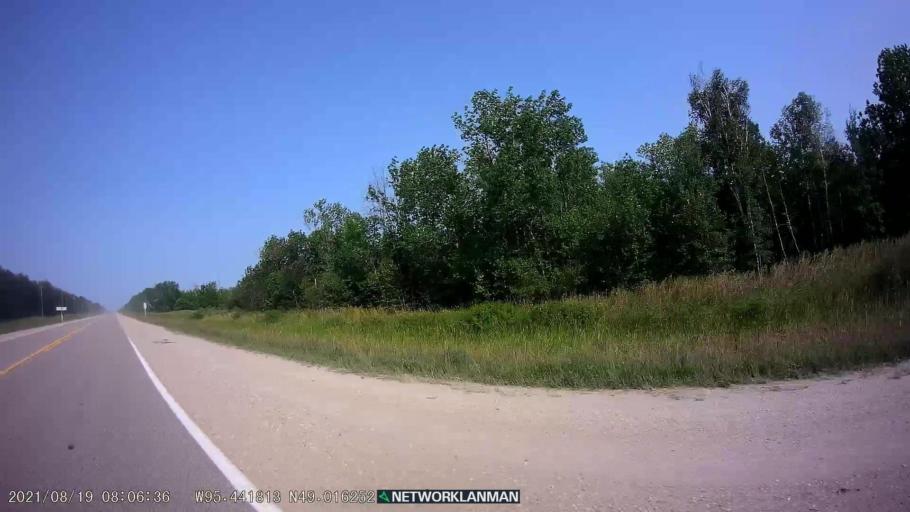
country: US
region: Minnesota
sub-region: Roseau County
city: Warroad
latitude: 49.0165
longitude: -95.4431
